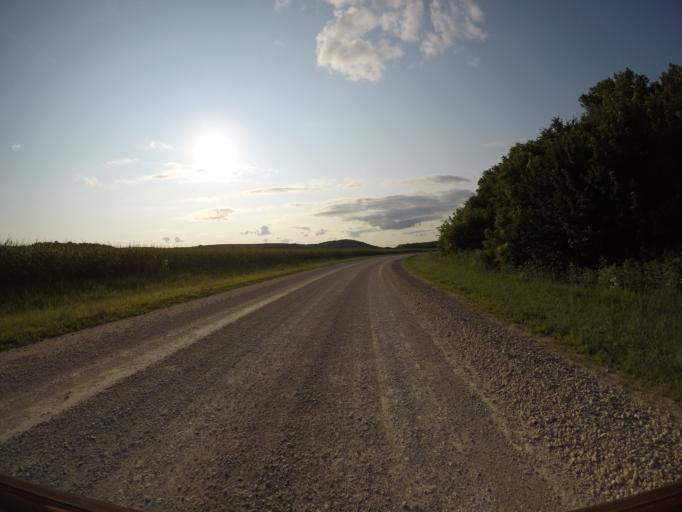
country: US
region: Kansas
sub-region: Wabaunsee County
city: Alma
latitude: 38.9521
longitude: -96.2473
